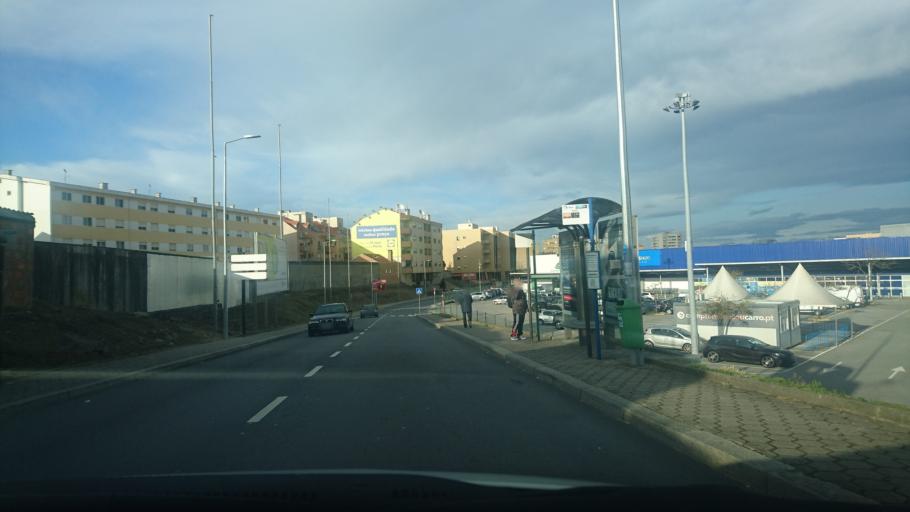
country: PT
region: Porto
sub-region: Vila Nova de Gaia
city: Vila Nova de Gaia
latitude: 41.1203
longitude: -8.6266
